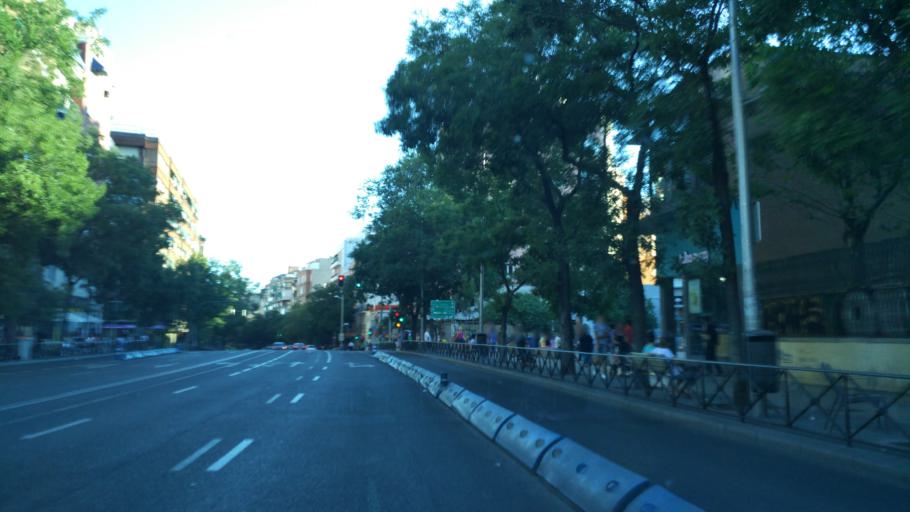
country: ES
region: Madrid
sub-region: Provincia de Madrid
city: Tetuan de las Victorias
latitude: 40.4583
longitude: -3.7009
